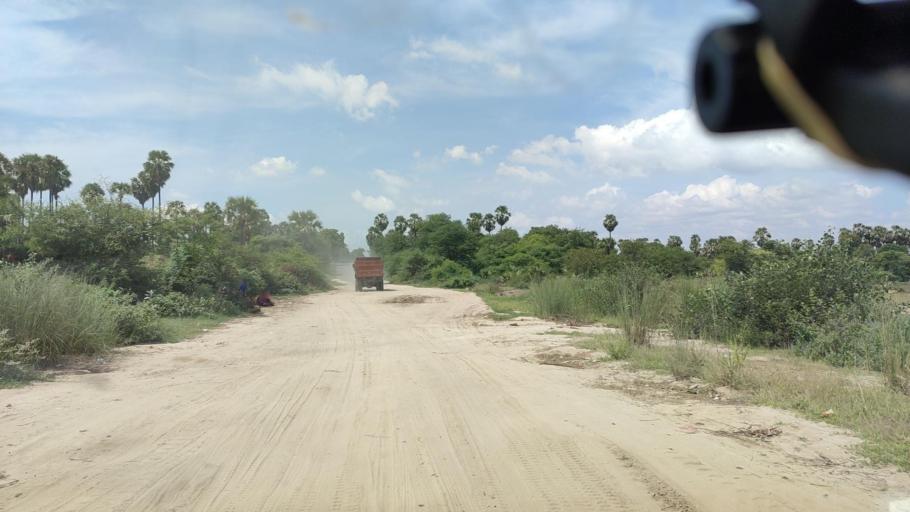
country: MM
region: Magway
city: Pakokku
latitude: 21.2942
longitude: 95.1407
